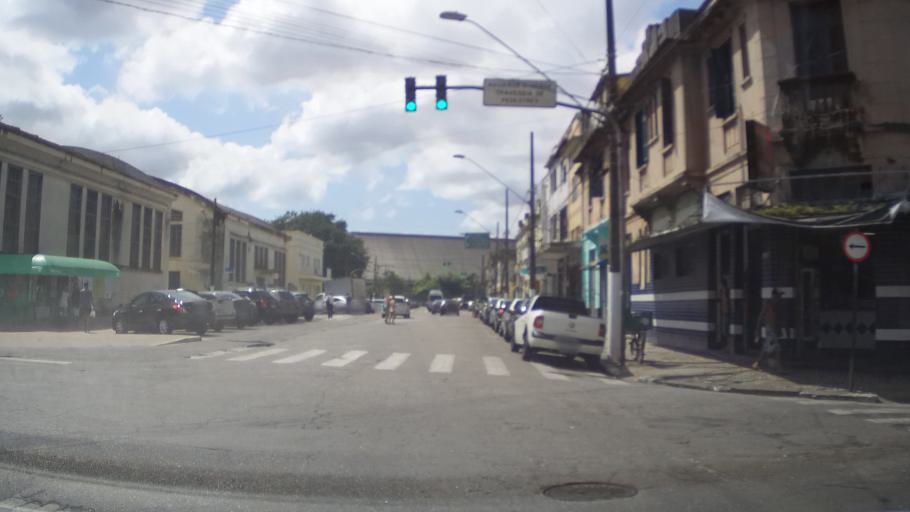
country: BR
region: Sao Paulo
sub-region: Santos
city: Santos
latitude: -23.9408
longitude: -46.3195
